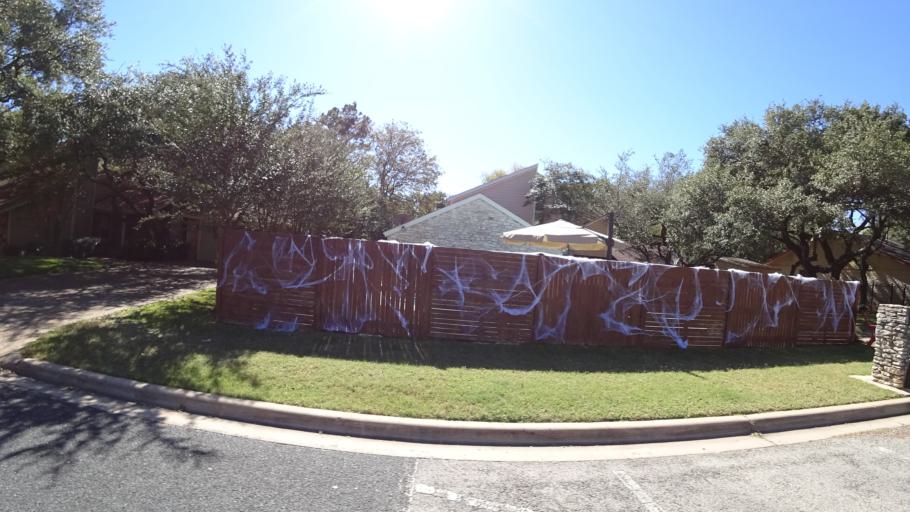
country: US
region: Texas
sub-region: Travis County
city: West Lake Hills
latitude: 30.3634
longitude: -97.7581
